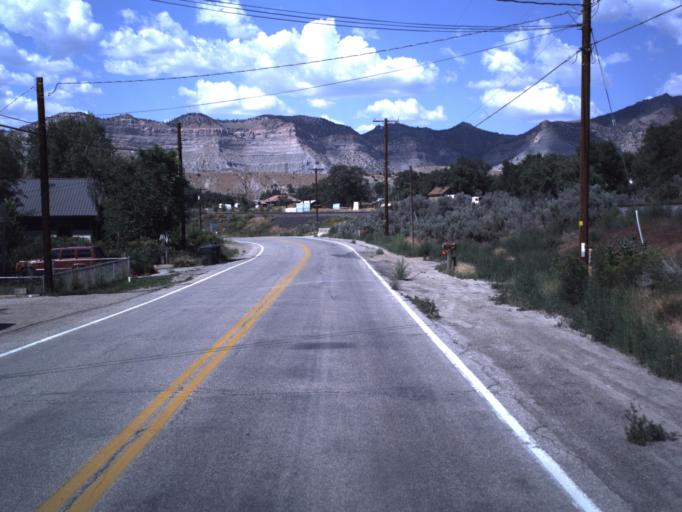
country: US
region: Utah
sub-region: Carbon County
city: Spring Glen
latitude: 39.6634
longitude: -110.8559
